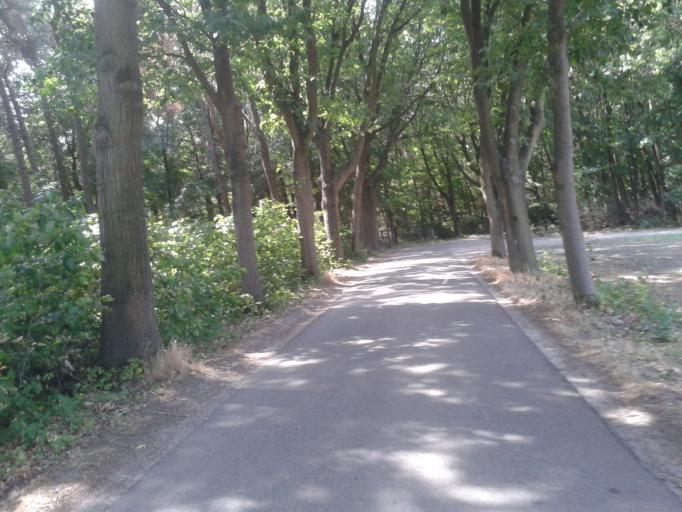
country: NL
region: North Brabant
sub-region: Gemeente Oisterwijk
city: Oisterwijk
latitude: 51.5652
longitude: 5.1741
